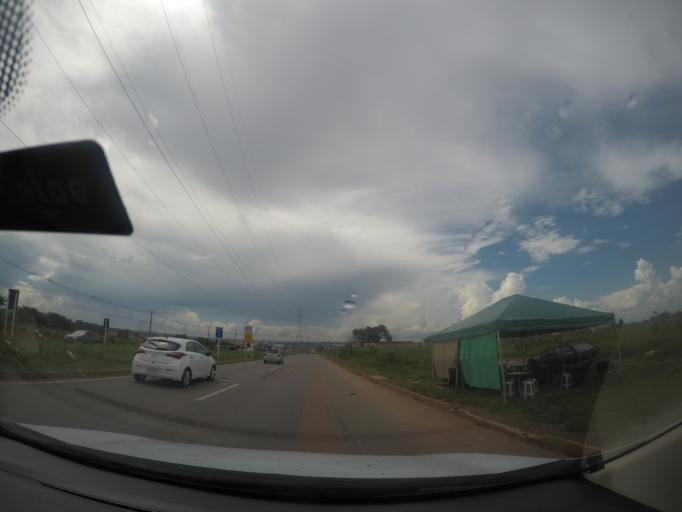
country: BR
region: Goias
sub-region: Goiania
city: Goiania
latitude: -16.7455
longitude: -49.3431
